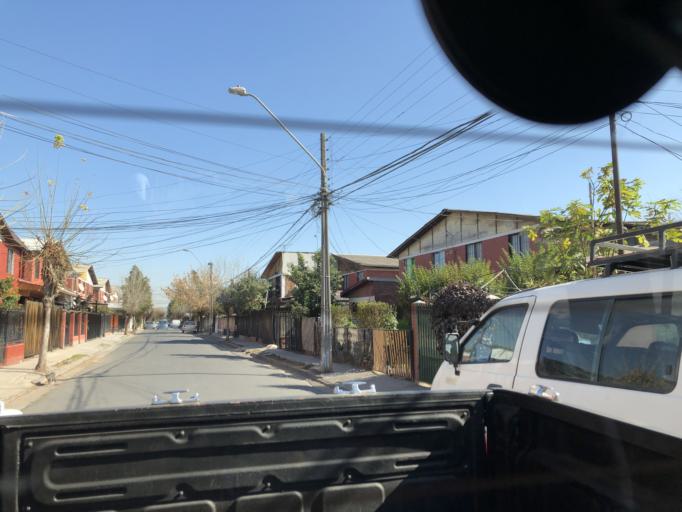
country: CL
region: Santiago Metropolitan
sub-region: Provincia de Cordillera
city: Puente Alto
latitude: -33.5653
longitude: -70.5752
